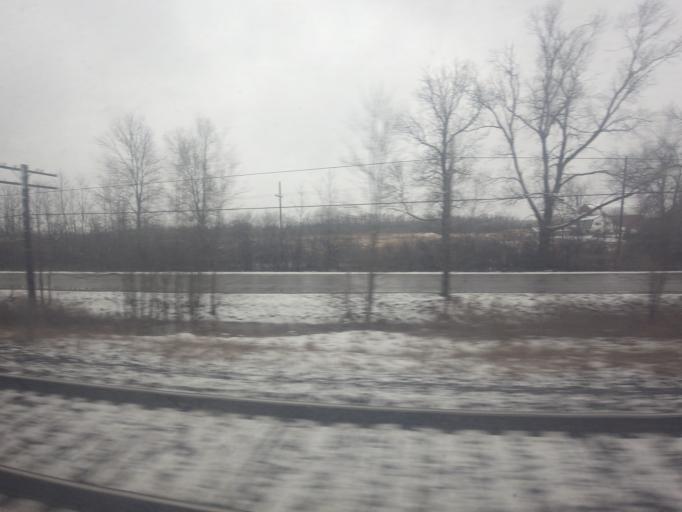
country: CA
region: Ontario
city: Belleville
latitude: 44.1597
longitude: -77.4443
